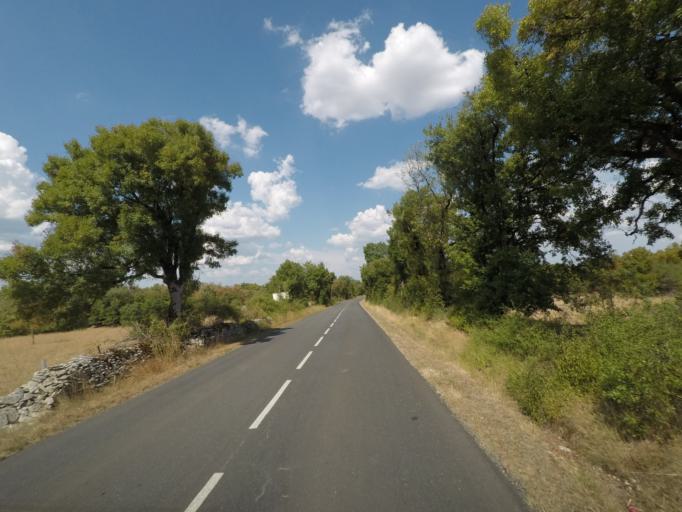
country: FR
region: Midi-Pyrenees
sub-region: Departement du Lot
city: Gramat
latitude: 44.6785
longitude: 1.6008
